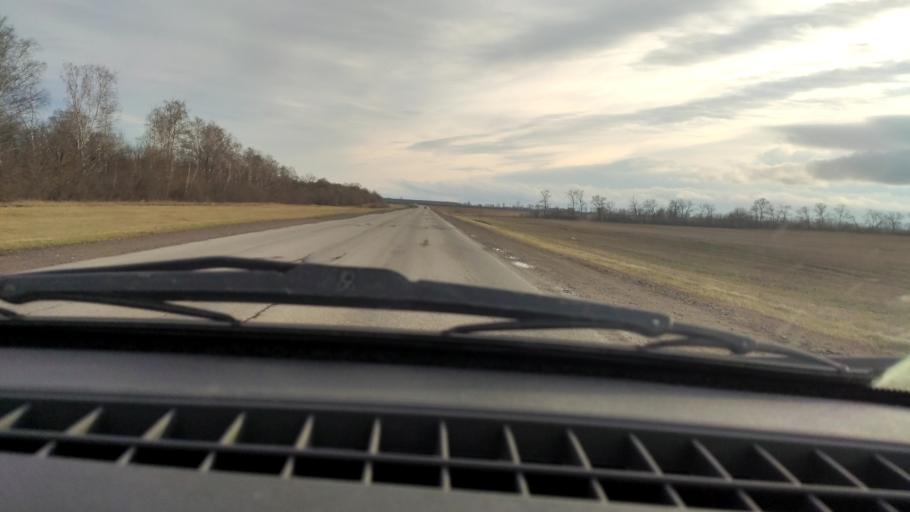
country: RU
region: Bashkortostan
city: Davlekanovo
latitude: 54.2829
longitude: 55.1113
